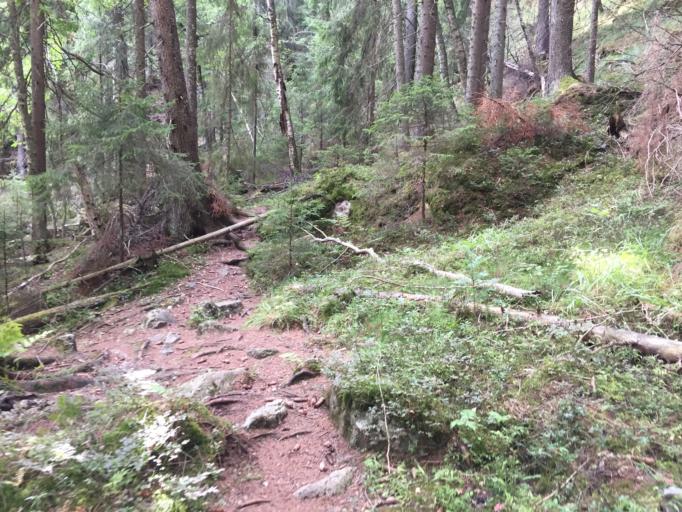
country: NO
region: Akershus
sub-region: Raelingen
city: Fjerdingby
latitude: 59.9113
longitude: 11.0344
